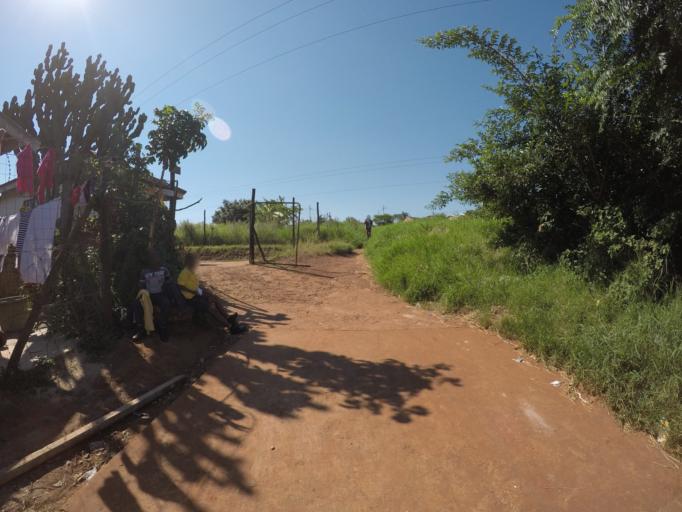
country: ZA
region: KwaZulu-Natal
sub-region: uThungulu District Municipality
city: Empangeni
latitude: -28.7751
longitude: 31.8800
